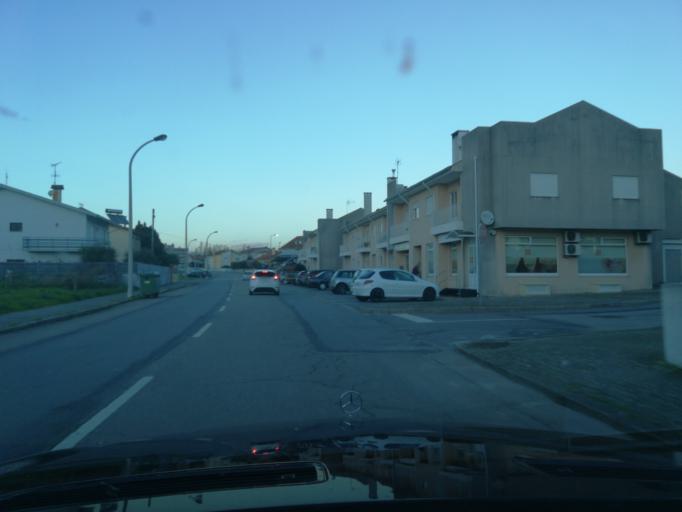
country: PT
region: Aveiro
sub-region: Estarreja
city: Estarreja
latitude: 40.7595
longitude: -8.5730
